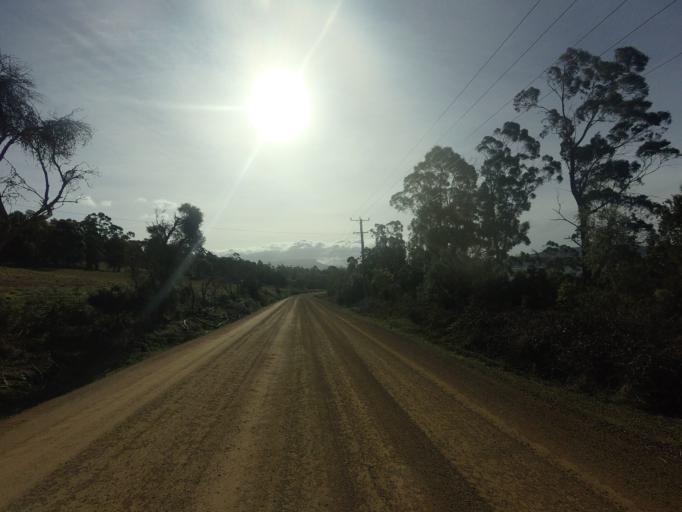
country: AU
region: Tasmania
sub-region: Kingborough
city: Kettering
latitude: -43.0875
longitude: 147.2644
